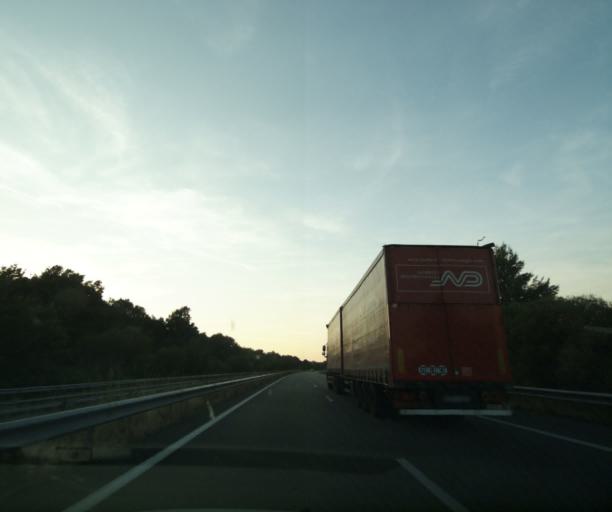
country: FR
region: Aquitaine
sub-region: Departement du Lot-et-Garonne
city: Fourques-sur-Garonne
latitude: 44.3840
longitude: 0.2045
